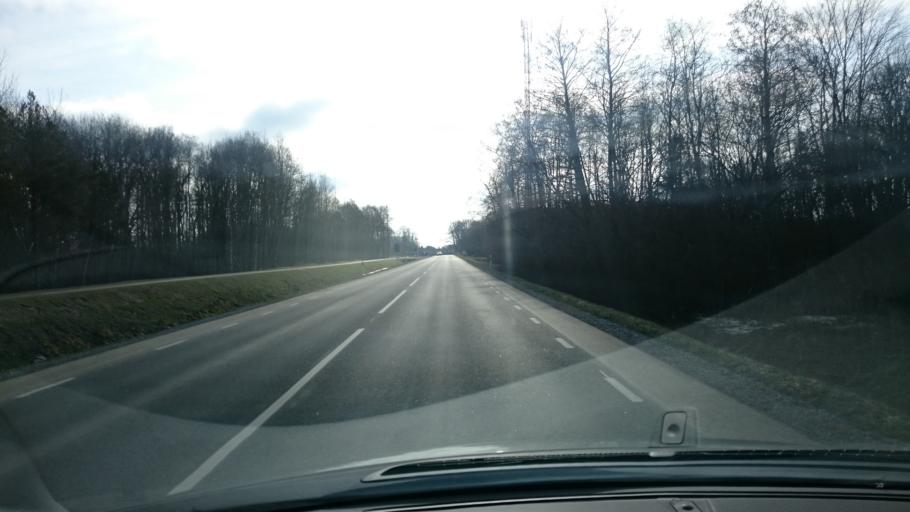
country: EE
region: Harju
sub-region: Paldiski linn
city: Paldiski
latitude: 59.3825
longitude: 24.2358
